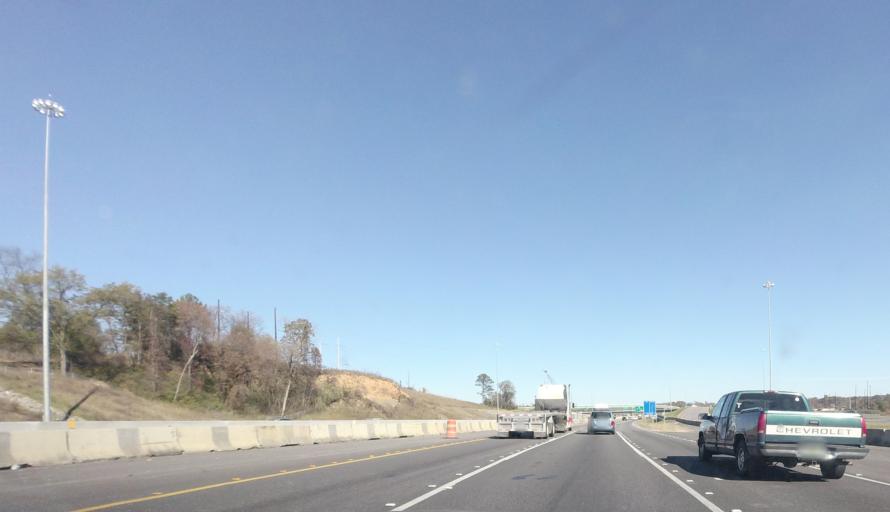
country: US
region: Alabama
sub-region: Jefferson County
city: Fultondale
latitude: 33.5668
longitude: -86.8224
